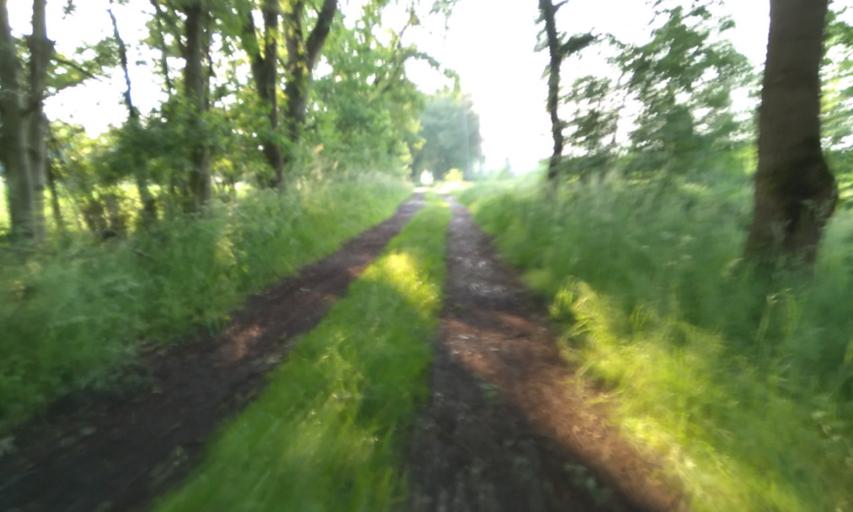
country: DE
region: Lower Saxony
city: Apensen
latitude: 53.4256
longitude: 9.5673
